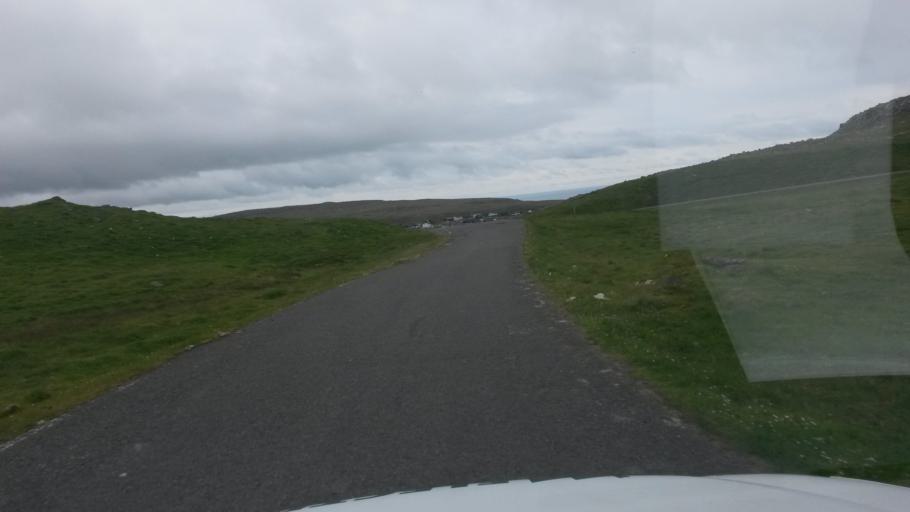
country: FO
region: Streymoy
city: Argir
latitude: 61.9949
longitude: -6.8470
